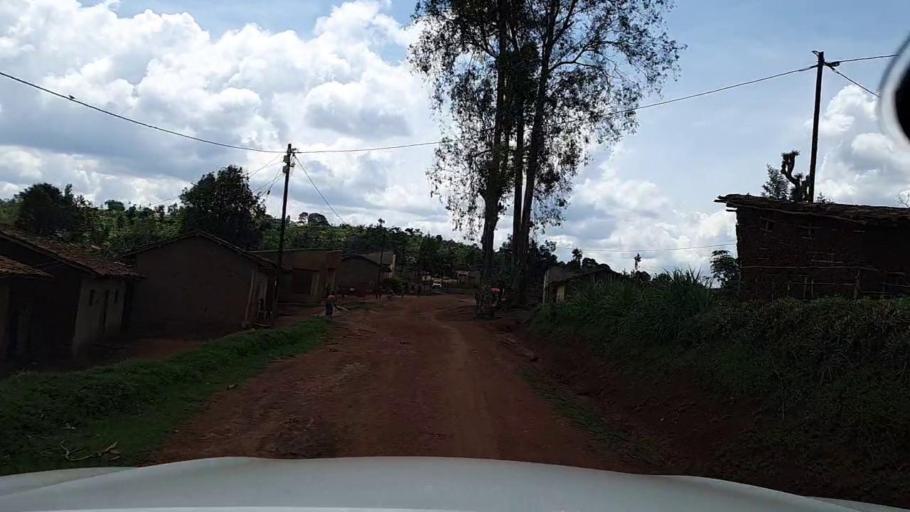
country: RW
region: Southern Province
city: Butare
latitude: -2.7612
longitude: 29.7442
